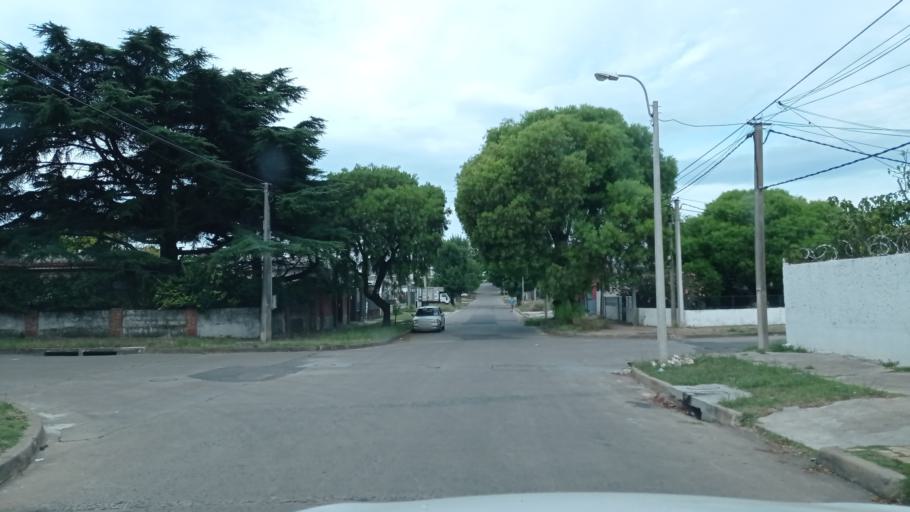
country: UY
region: Montevideo
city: Montevideo
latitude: -34.8390
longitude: -56.2057
